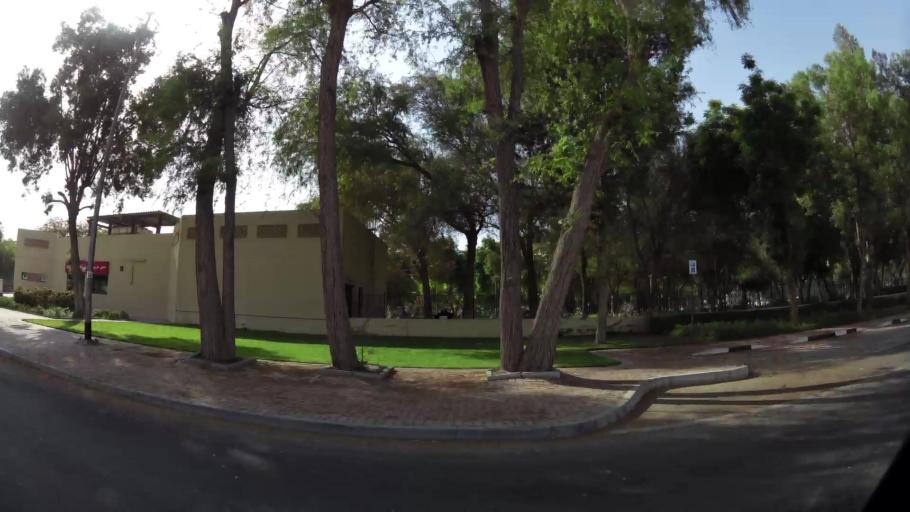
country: AE
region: Dubai
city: Dubai
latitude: 25.1500
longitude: 55.3246
